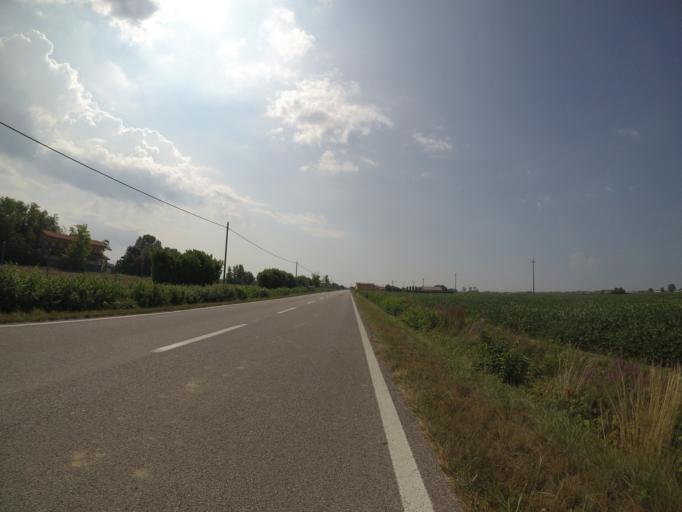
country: IT
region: Friuli Venezia Giulia
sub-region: Provincia di Udine
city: Pertegada
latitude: 45.7447
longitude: 13.0617
